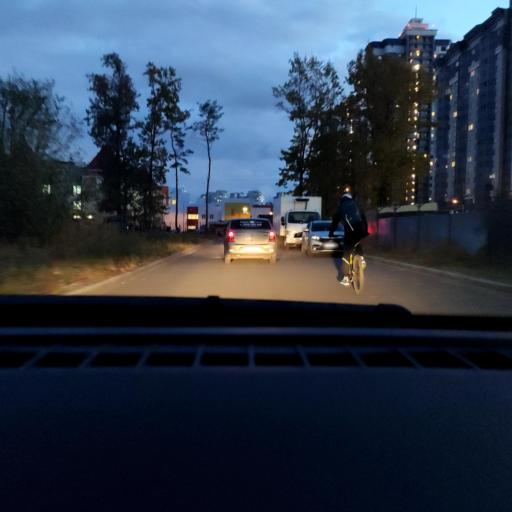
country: RU
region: Voronezj
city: Podgornoye
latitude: 51.7177
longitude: 39.1832
